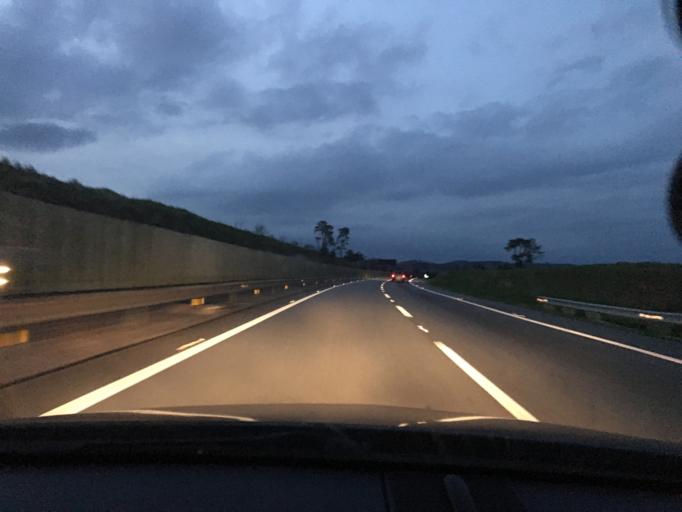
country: BR
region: Sao Paulo
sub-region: Santa Isabel
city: Santa Isabel
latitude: -23.3504
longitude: -46.1262
